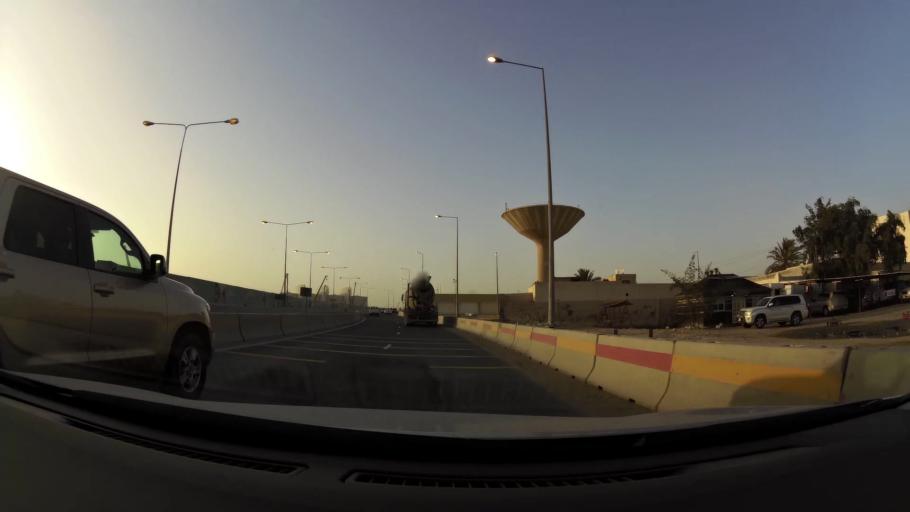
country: QA
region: Baladiyat ar Rayyan
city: Ar Rayyan
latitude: 25.3141
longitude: 51.4516
